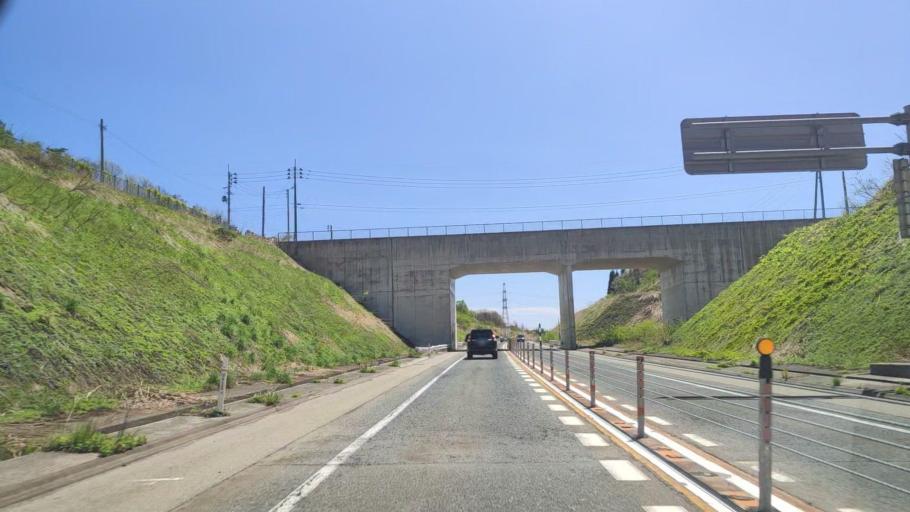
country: JP
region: Yamagata
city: Shinjo
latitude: 38.7226
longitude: 140.3084
